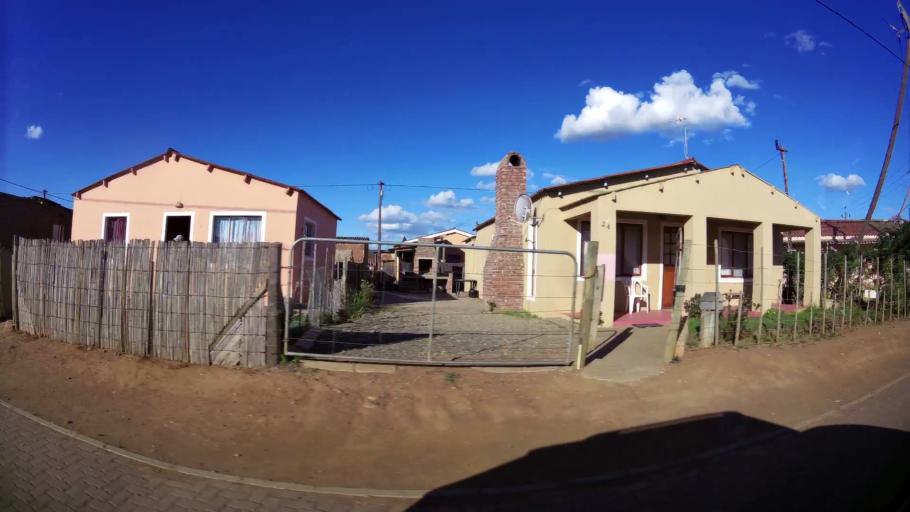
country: ZA
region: Western Cape
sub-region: Eden District Municipality
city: Riversdale
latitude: -34.1073
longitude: 20.9620
